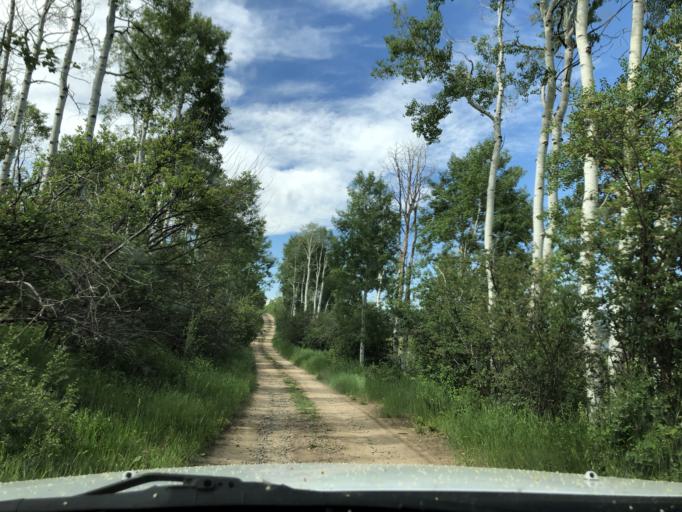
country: US
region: Colorado
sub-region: Delta County
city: Paonia
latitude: 39.0335
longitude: -107.3406
